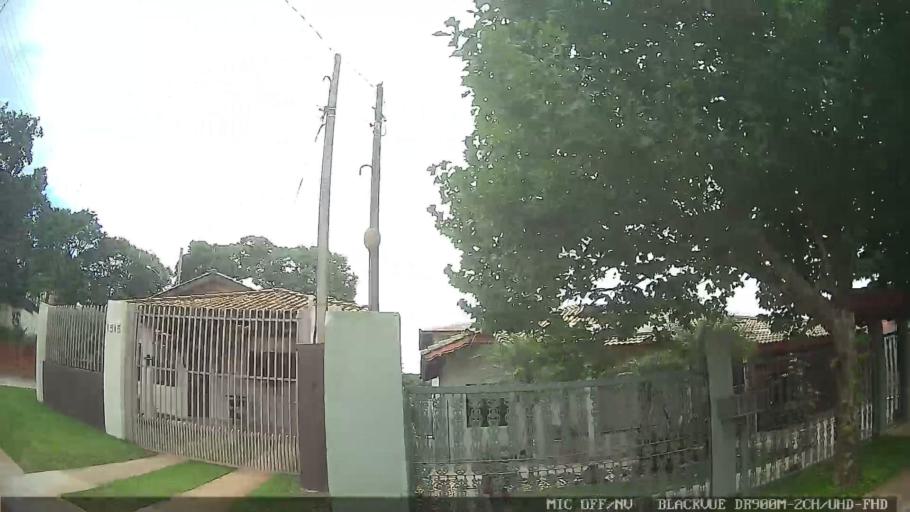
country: BR
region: Sao Paulo
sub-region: Atibaia
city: Atibaia
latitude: -23.1427
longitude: -46.5672
